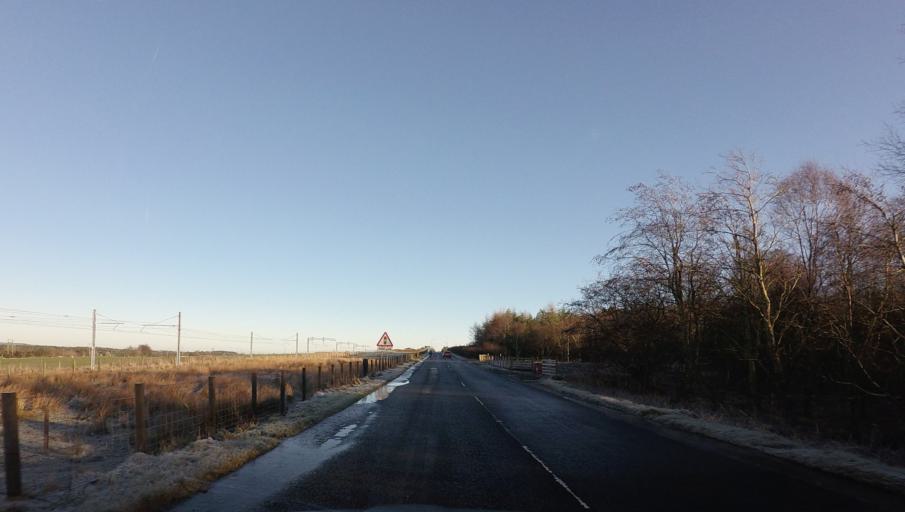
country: GB
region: Scotland
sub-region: West Lothian
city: Fauldhouse
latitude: 55.8249
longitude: -3.6749
